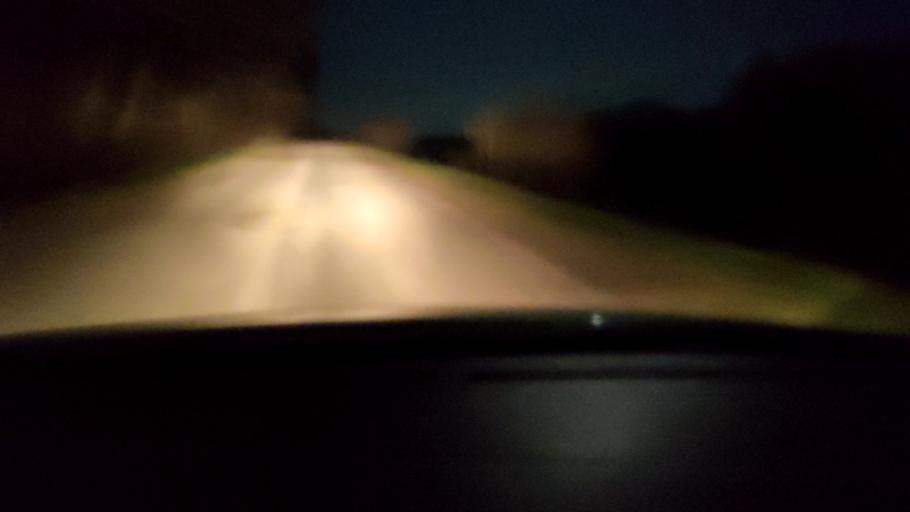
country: RU
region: Voronezj
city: Uryv-Pokrovka
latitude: 51.1258
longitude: 39.1159
